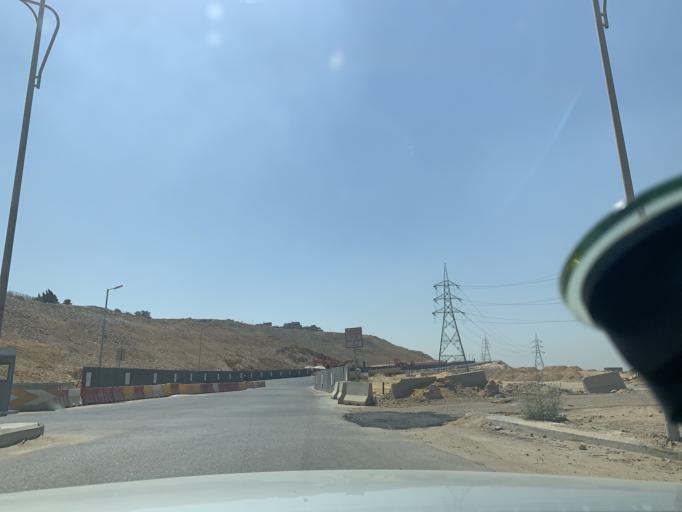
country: EG
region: Muhafazat al Qahirah
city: Cairo
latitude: 30.0149
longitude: 31.3405
